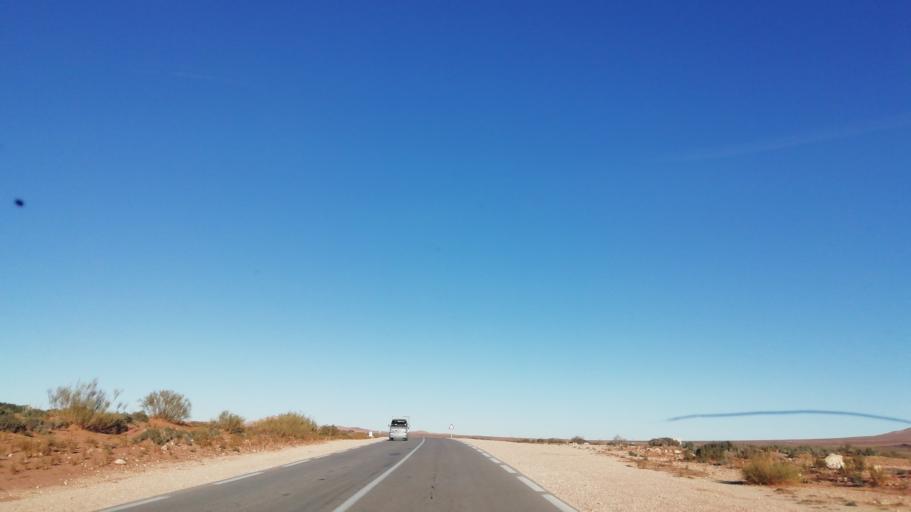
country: DZ
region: El Bayadh
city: El Abiodh Sidi Cheikh
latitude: 33.0948
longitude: 0.2011
